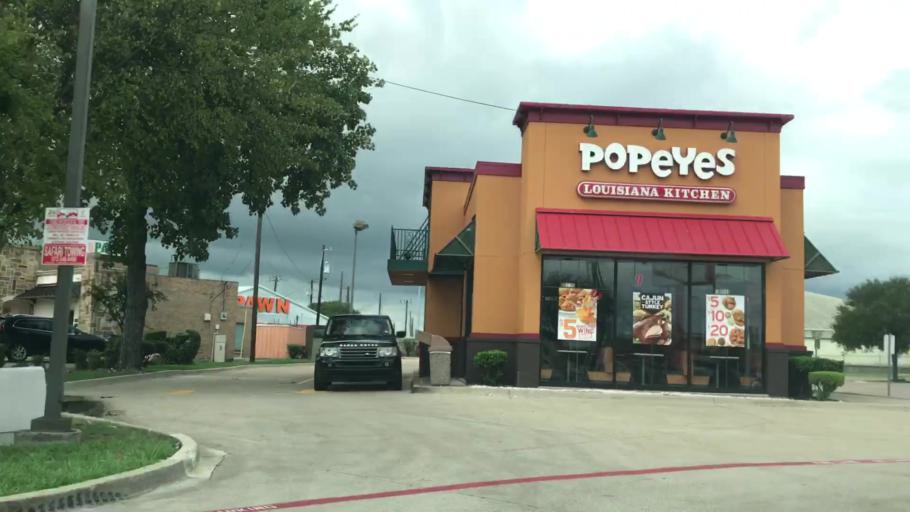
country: US
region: Texas
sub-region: Dallas County
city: Garland
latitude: 32.8797
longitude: -96.6222
